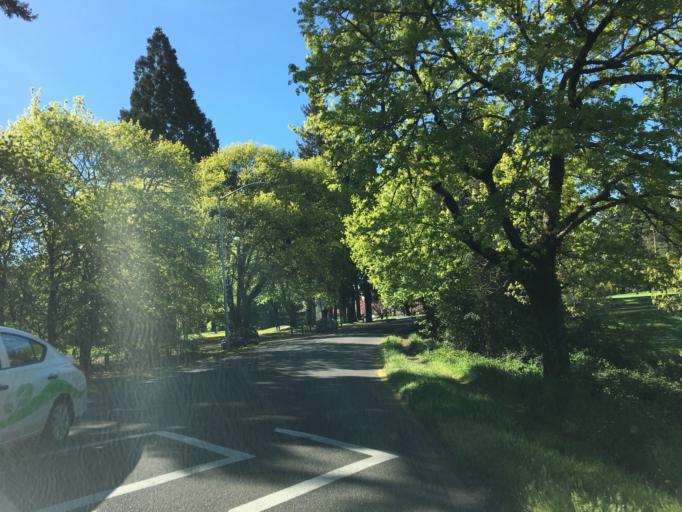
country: US
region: Oregon
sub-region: Multnomah County
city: Lents
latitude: 45.5403
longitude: -122.5897
